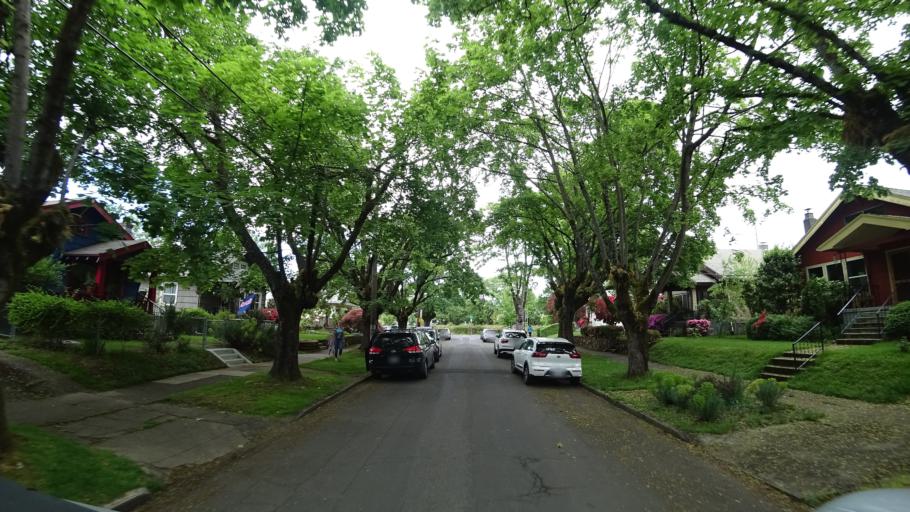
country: US
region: Oregon
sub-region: Multnomah County
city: Portland
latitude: 45.5060
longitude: -122.6494
